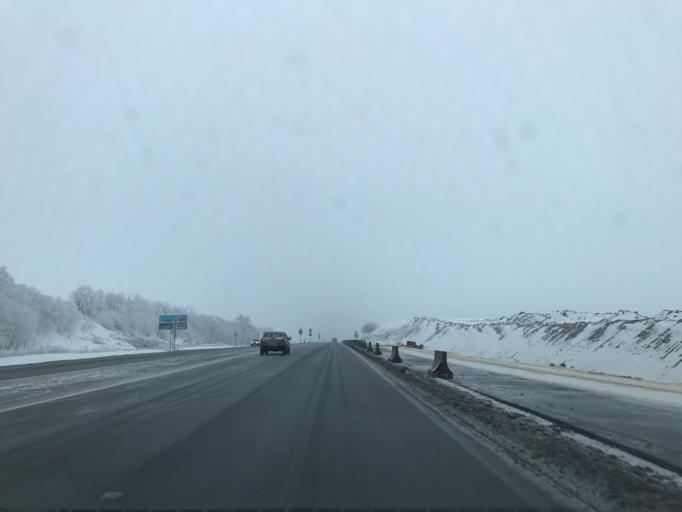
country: RU
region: Rostov
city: Grushevskaya
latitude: 47.5092
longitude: 39.9707
